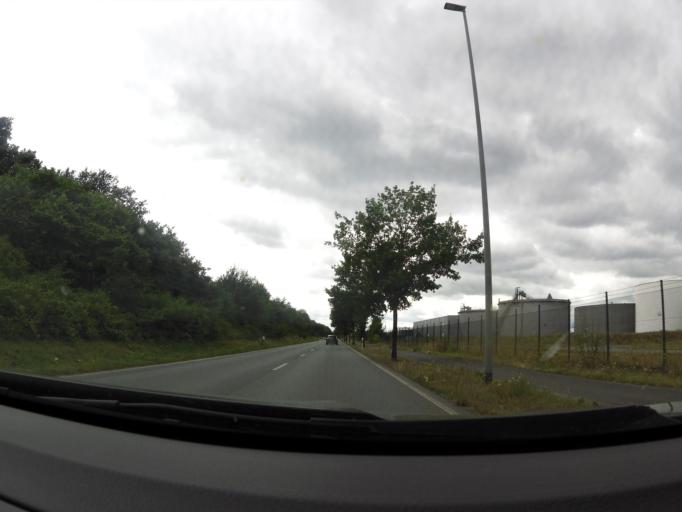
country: DE
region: North Rhine-Westphalia
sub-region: Regierungsbezirk Dusseldorf
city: Voerde
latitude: 51.6296
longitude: 6.7014
